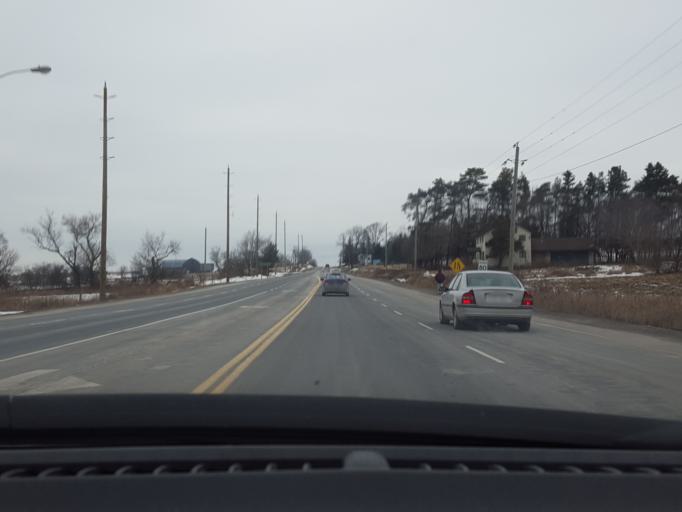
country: CA
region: Ontario
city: Newmarket
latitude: 44.1443
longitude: -79.4260
